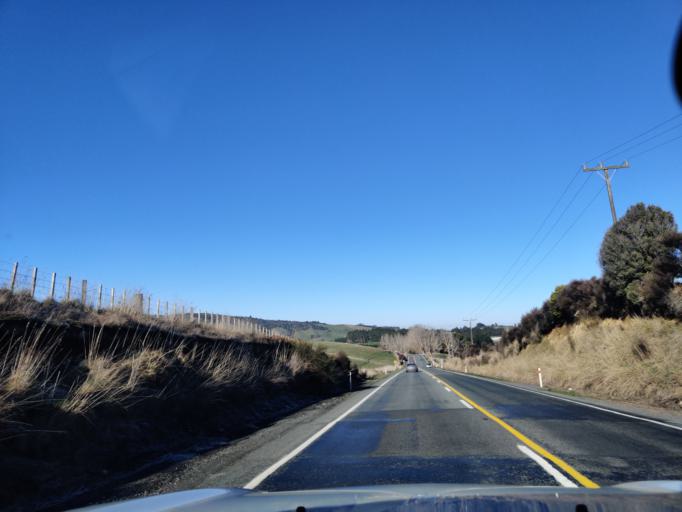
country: NZ
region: Manawatu-Wanganui
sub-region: Ruapehu District
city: Waiouru
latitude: -39.5309
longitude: 175.6830
